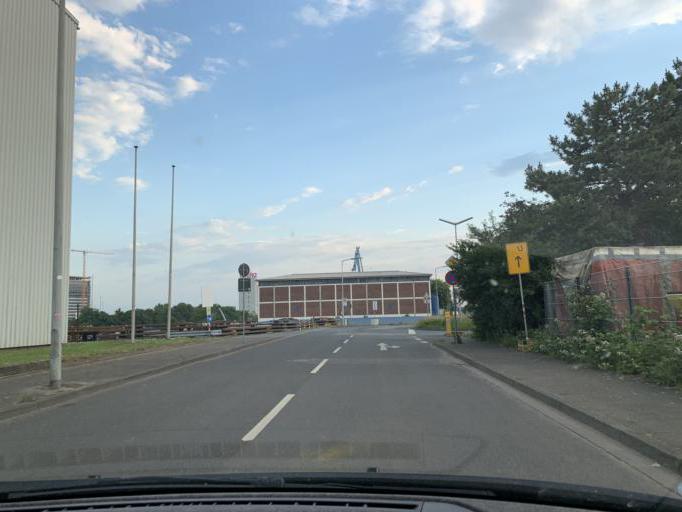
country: DE
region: North Rhine-Westphalia
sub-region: Regierungsbezirk Dusseldorf
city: Dusseldorf
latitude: 51.2213
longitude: 6.7452
